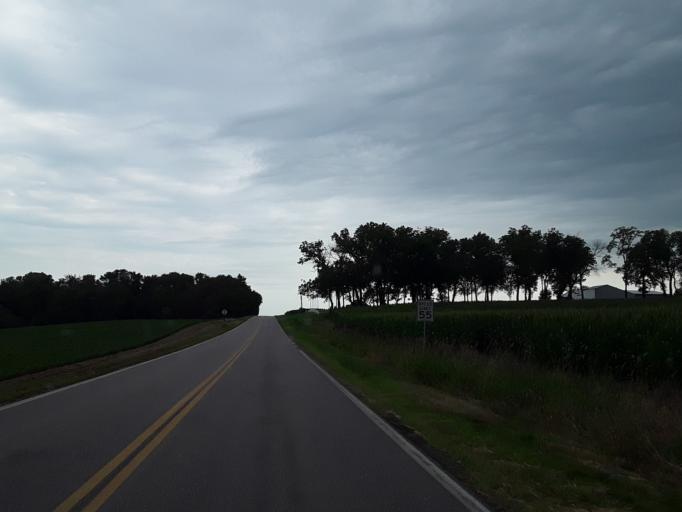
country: US
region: Nebraska
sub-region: Saunders County
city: Yutan
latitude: 41.2327
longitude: -96.3971
